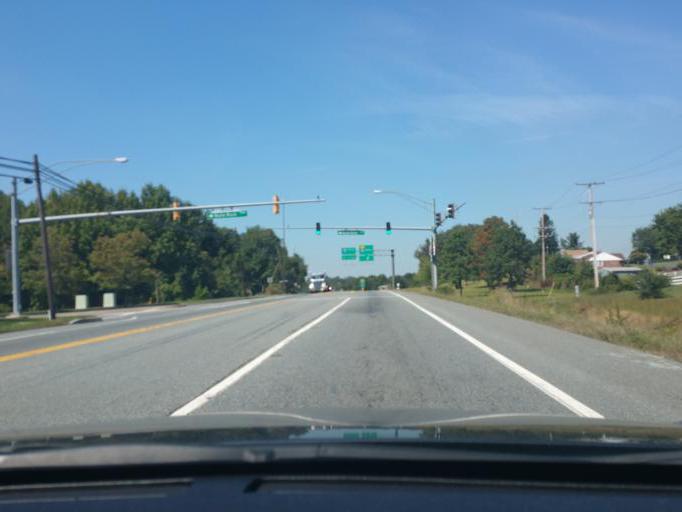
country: US
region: Maryland
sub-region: Harford County
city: Havre de Grace
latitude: 39.5679
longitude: -76.1304
